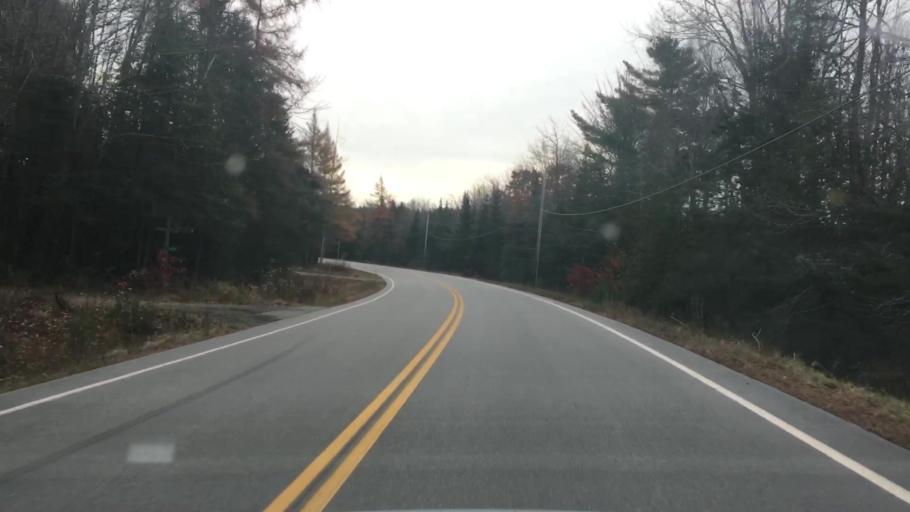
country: US
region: Maine
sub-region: Hancock County
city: Penobscot
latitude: 44.5044
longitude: -68.6553
